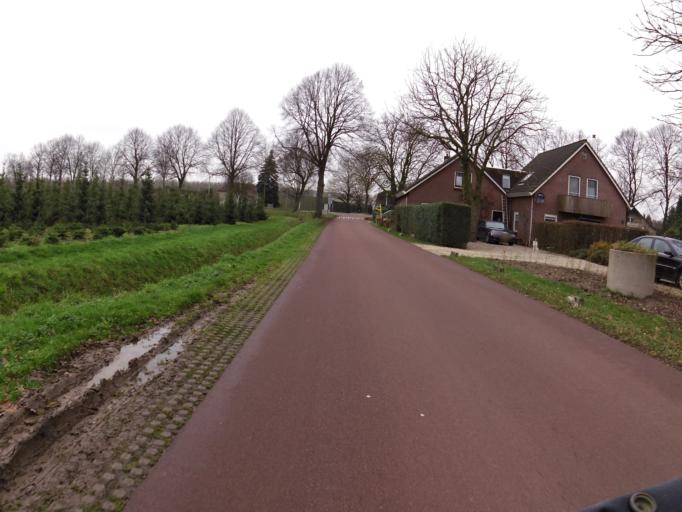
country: NL
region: Gelderland
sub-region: Gemeente Overbetuwe
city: Elst
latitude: 51.8904
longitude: 5.8712
